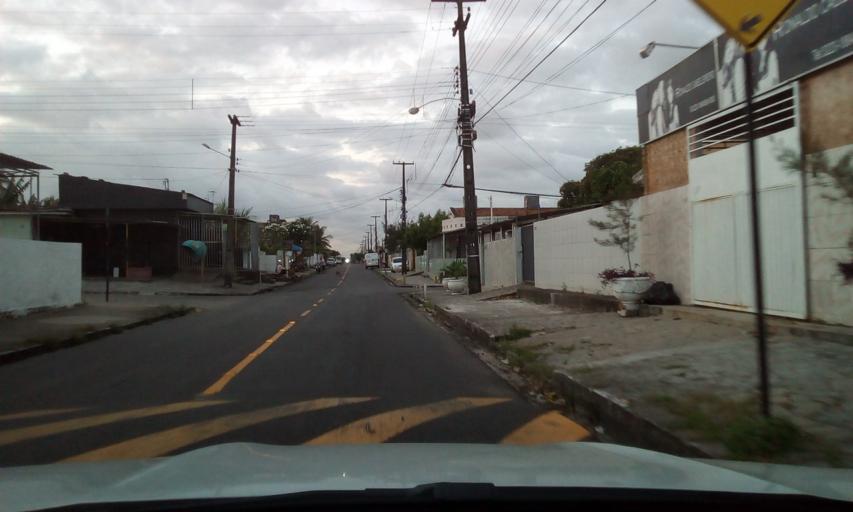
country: BR
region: Paraiba
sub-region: Joao Pessoa
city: Joao Pessoa
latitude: -7.1546
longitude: -34.8699
